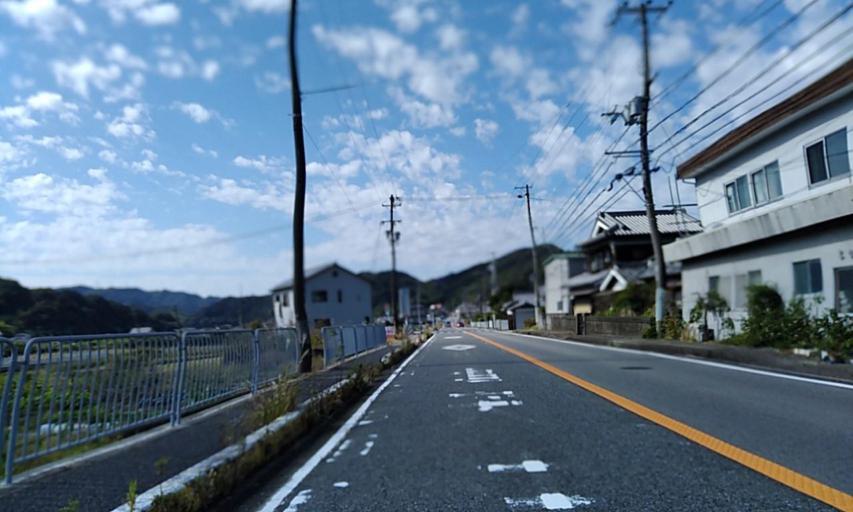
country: JP
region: Wakayama
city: Gobo
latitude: 33.9724
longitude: 135.1346
